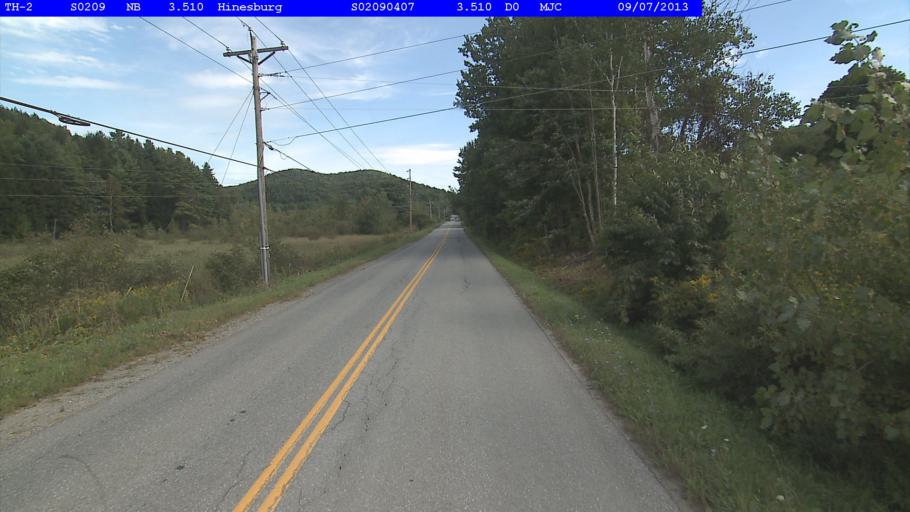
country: US
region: Vermont
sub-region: Chittenden County
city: Hinesburg
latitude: 44.3615
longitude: -73.0736
